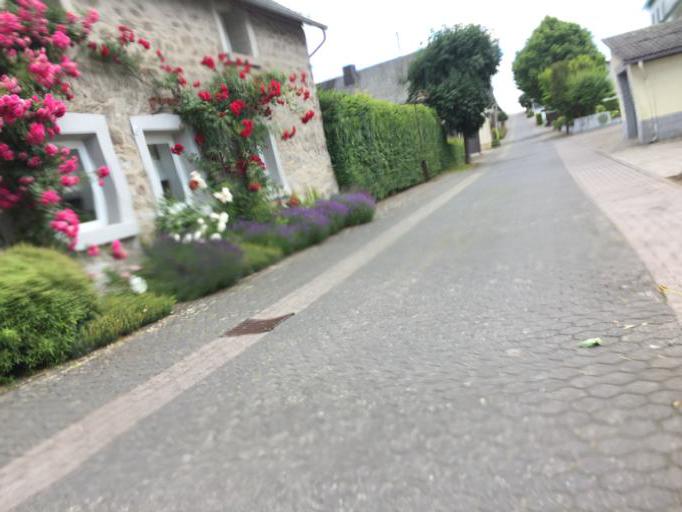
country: DE
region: Rheinland-Pfalz
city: Ruppach-Goldhausen
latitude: 50.4789
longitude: 7.9001
